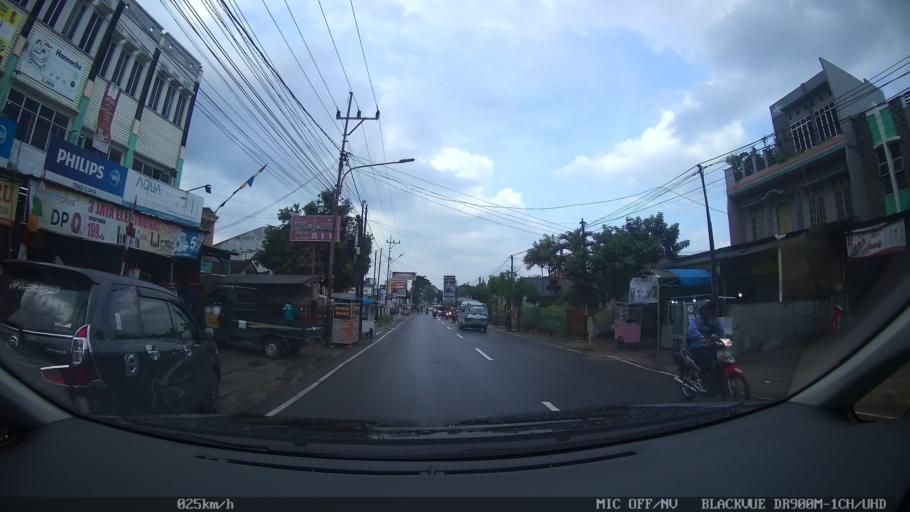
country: ID
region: Lampung
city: Kedaton
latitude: -5.3857
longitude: 105.2933
